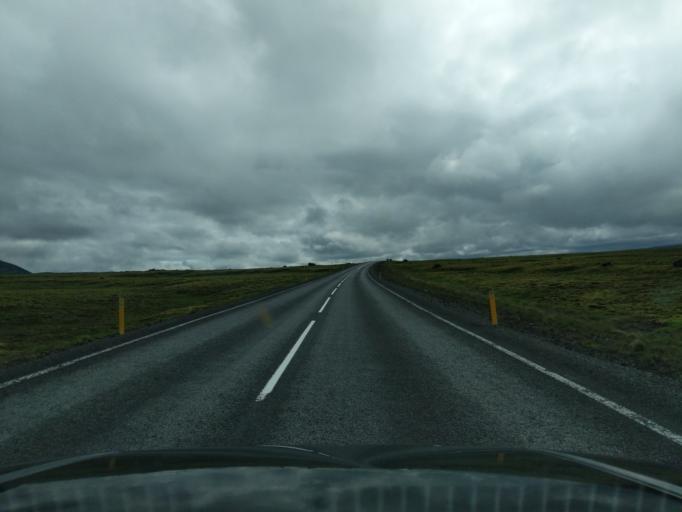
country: IS
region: South
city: Selfoss
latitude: 64.1961
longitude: -20.9811
